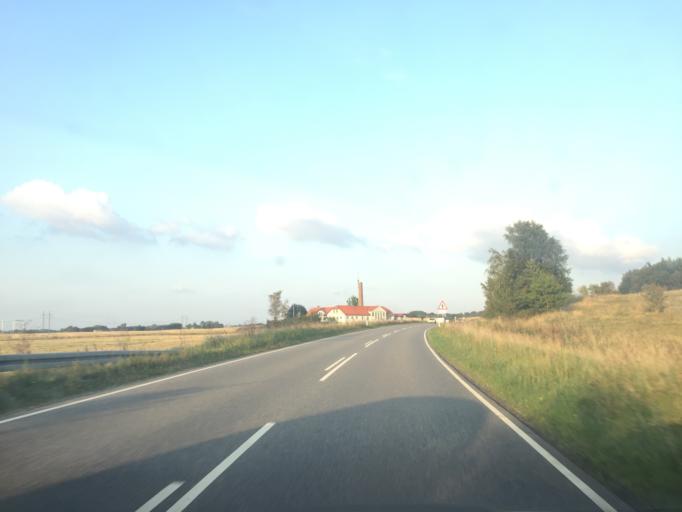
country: DK
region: Zealand
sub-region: Holbaek Kommune
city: Tollose
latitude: 55.5668
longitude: 11.7874
